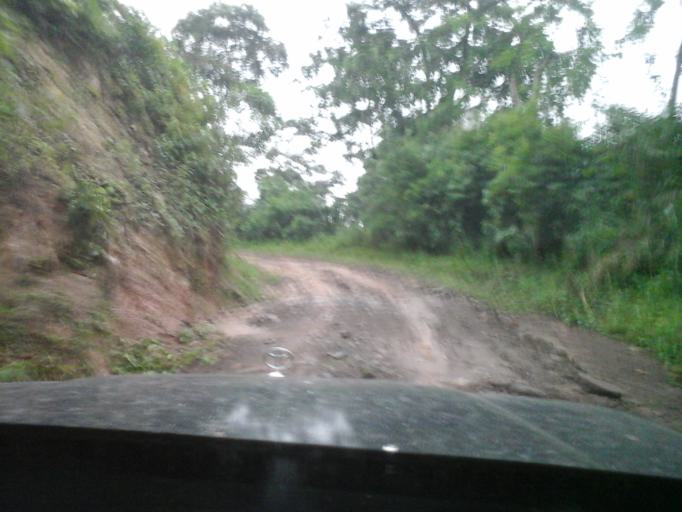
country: CO
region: Cesar
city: Agustin Codazzi
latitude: 9.9402
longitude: -73.1362
